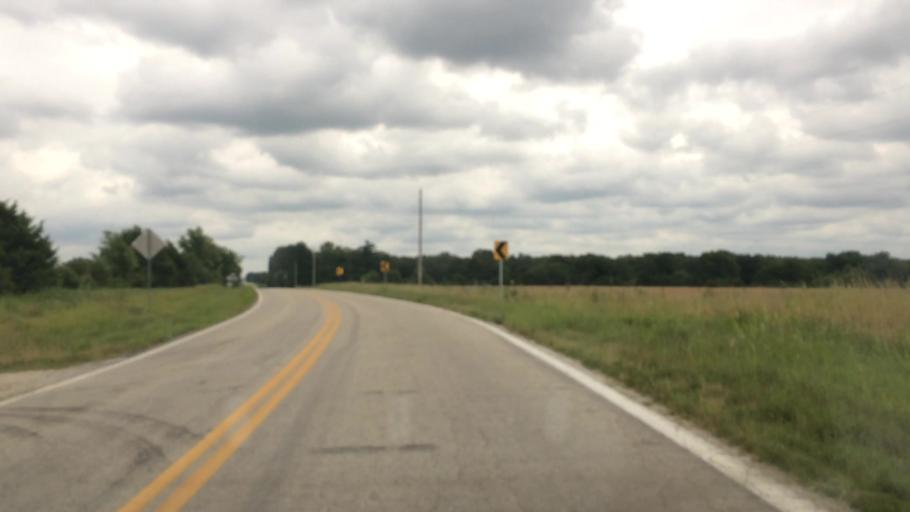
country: US
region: Missouri
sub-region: Greene County
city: Strafford
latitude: 37.3007
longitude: -93.1746
